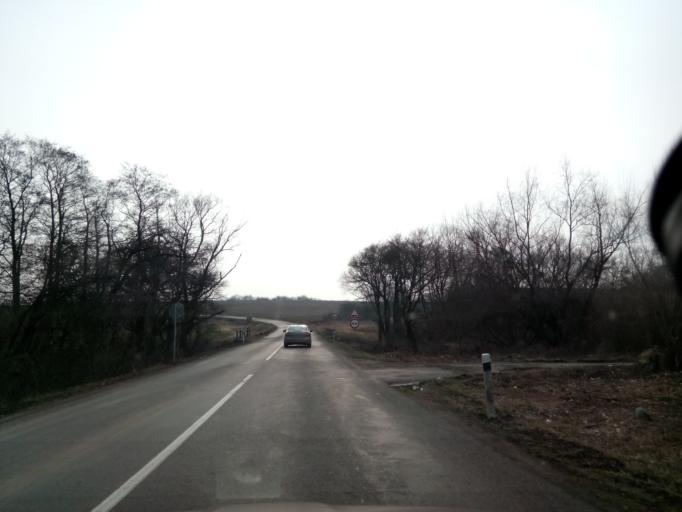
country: SK
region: Kosicky
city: Secovce
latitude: 48.6388
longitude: 21.5582
